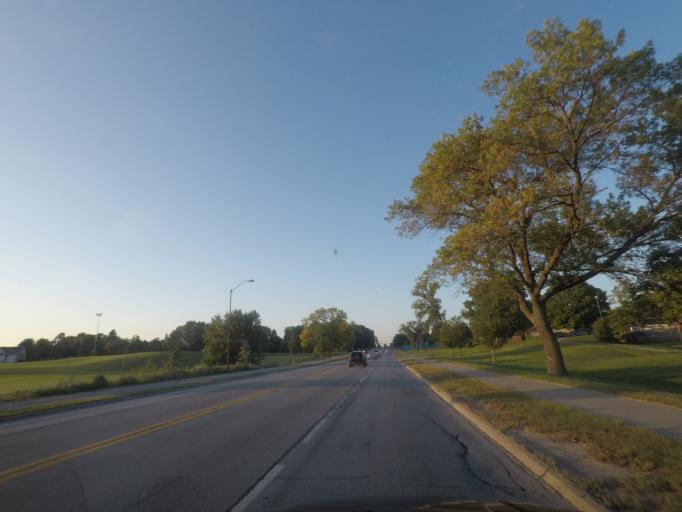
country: US
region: Iowa
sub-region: Story County
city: Ames
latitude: 42.0400
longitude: -93.6448
